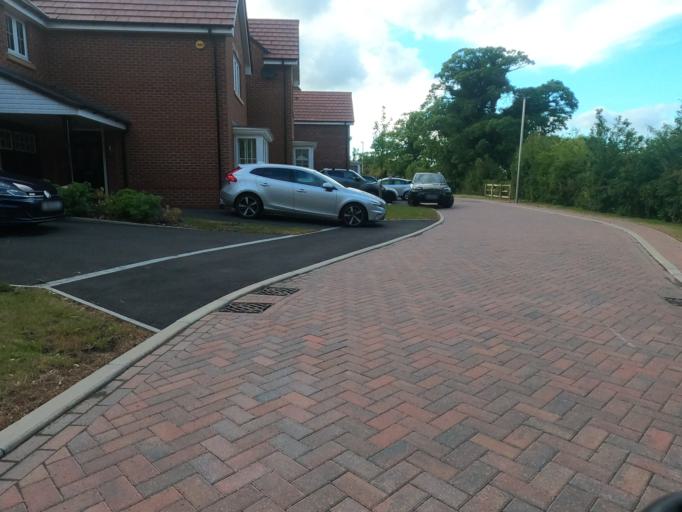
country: GB
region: England
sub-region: Cheshire West and Chester
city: Winsford
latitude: 53.2196
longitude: -2.5087
